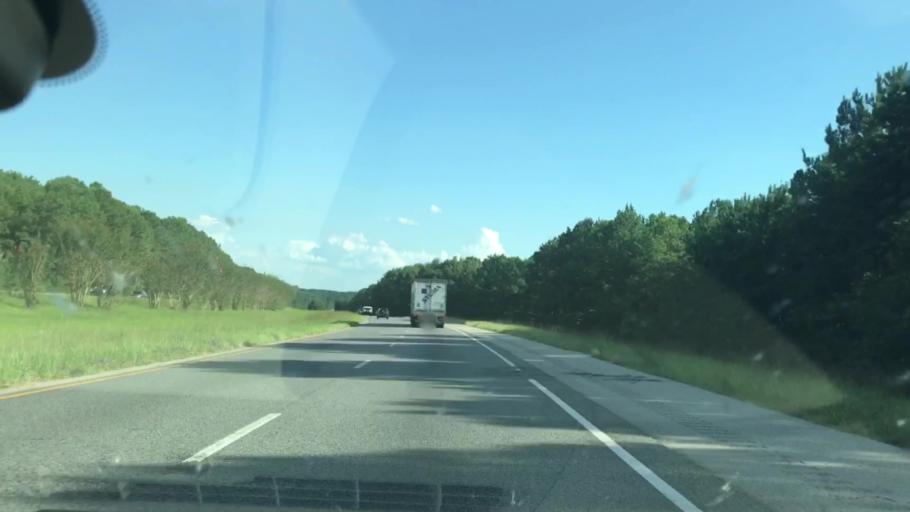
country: US
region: Georgia
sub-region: Troup County
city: La Grange
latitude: 32.9419
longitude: -84.9566
